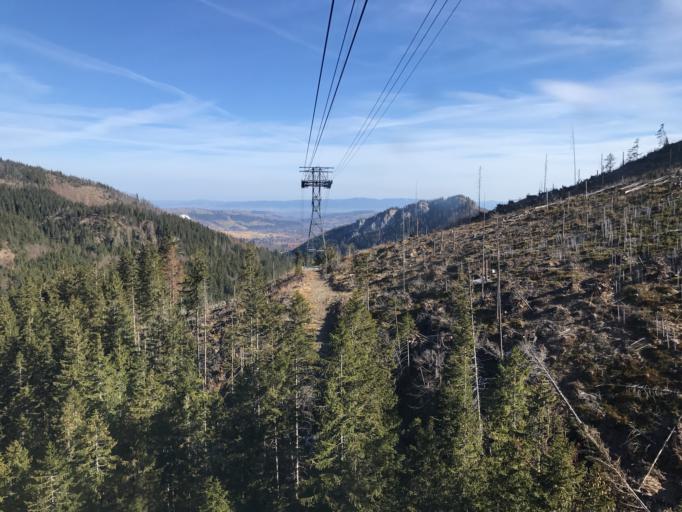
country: PL
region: Lesser Poland Voivodeship
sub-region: Powiat tatrzanski
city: Zakopane
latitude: 49.2592
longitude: 19.9761
